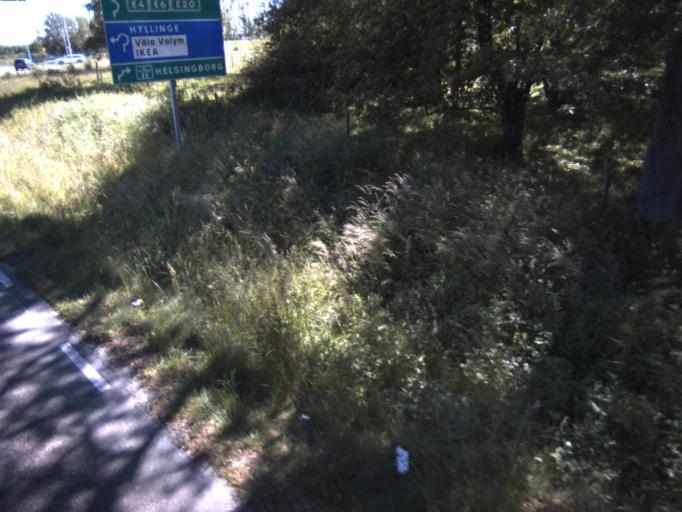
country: SE
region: Skane
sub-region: Helsingborg
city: Odakra
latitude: 56.0897
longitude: 12.7531
